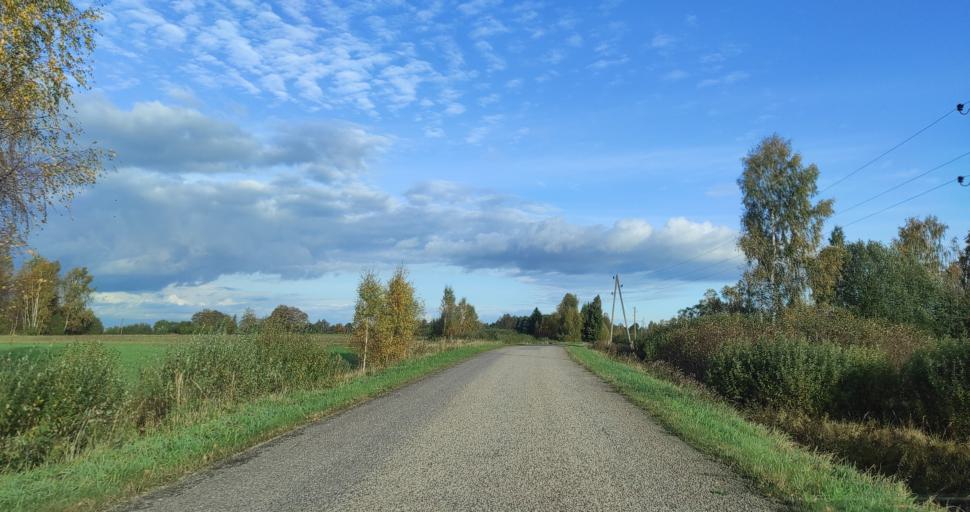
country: LV
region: Aizpute
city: Aizpute
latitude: 56.7537
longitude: 21.7831
